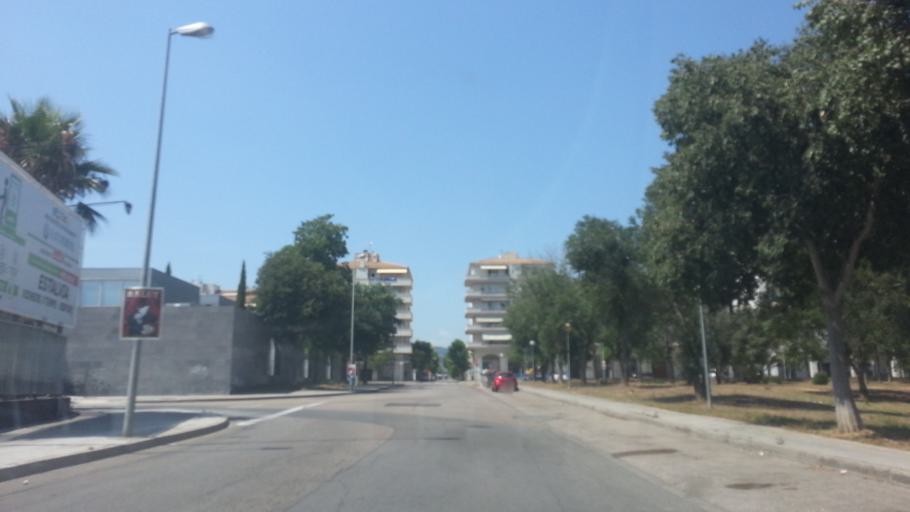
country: ES
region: Catalonia
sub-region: Provincia de Barcelona
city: Vilanova i la Geltru
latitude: 41.2229
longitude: 1.7369
